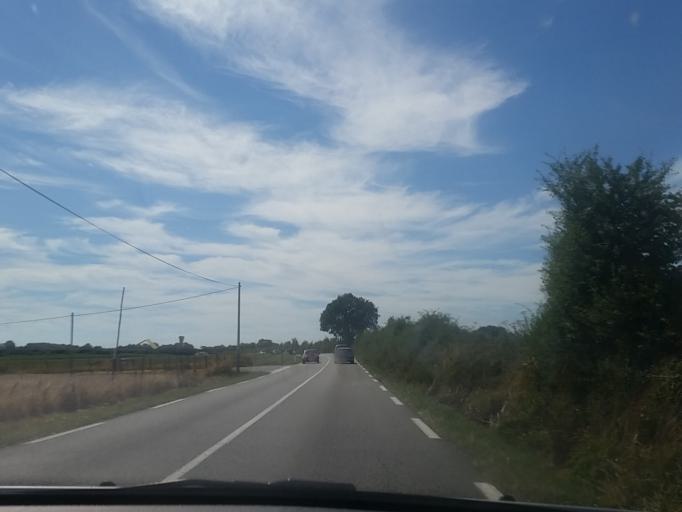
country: FR
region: Pays de la Loire
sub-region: Departement de la Loire-Atlantique
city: Vue
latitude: 47.1979
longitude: -1.9108
